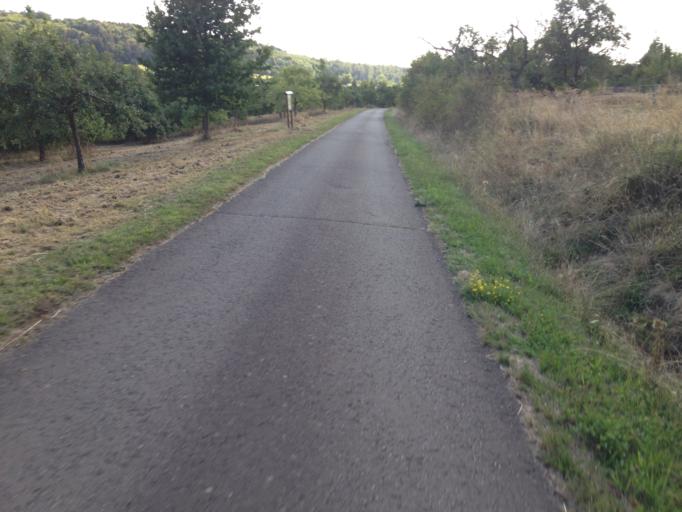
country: DE
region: Hesse
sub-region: Regierungsbezirk Giessen
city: Reiskirchen
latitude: 50.6212
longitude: 8.8567
